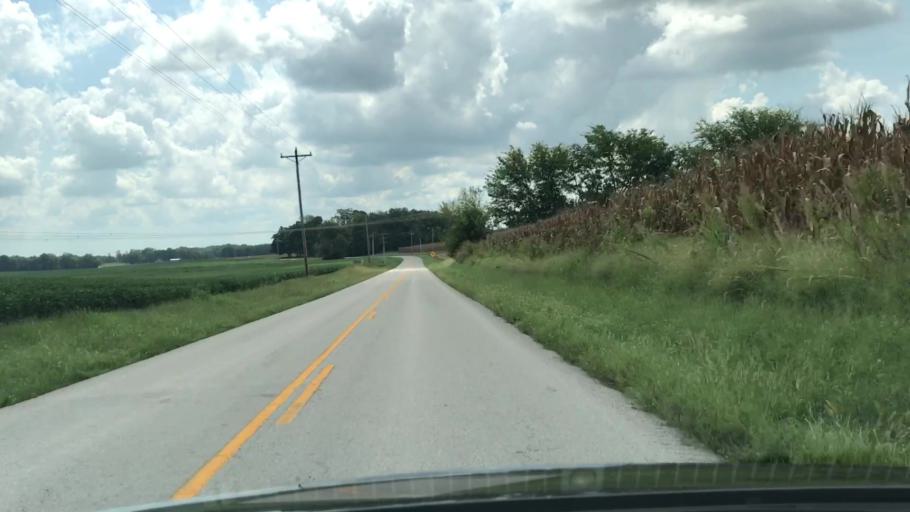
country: US
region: Kentucky
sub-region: Todd County
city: Elkton
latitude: 36.7748
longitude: -87.1185
